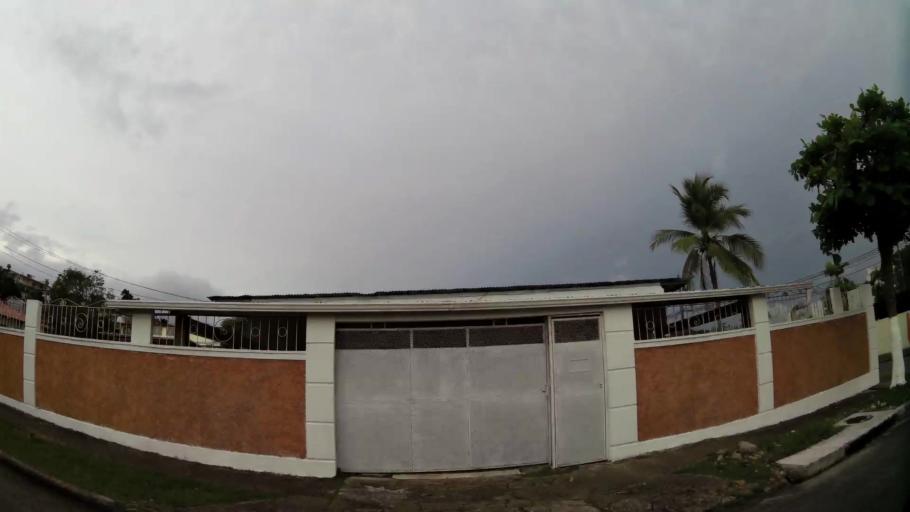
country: PA
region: Panama
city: Panama
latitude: 9.0180
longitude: -79.5277
